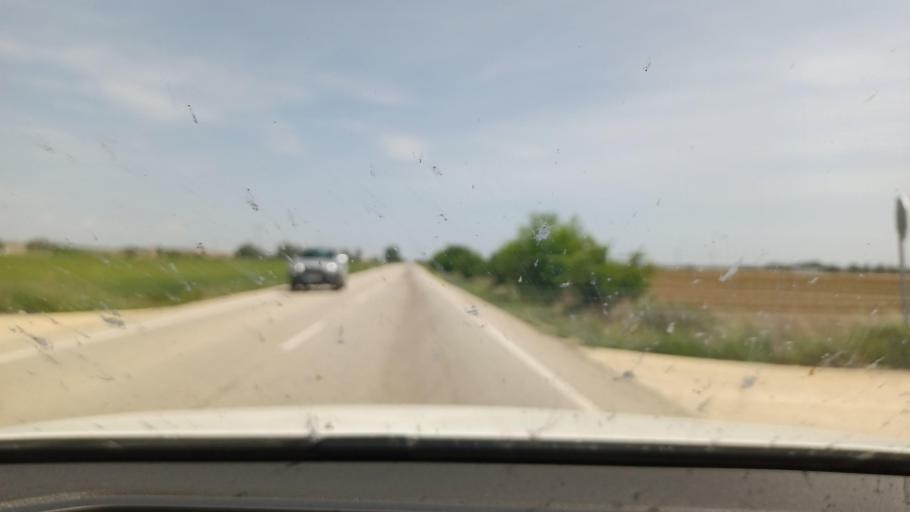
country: ES
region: Castille and Leon
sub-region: Provincia de Soria
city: Almazan
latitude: 41.4742
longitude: -2.5158
